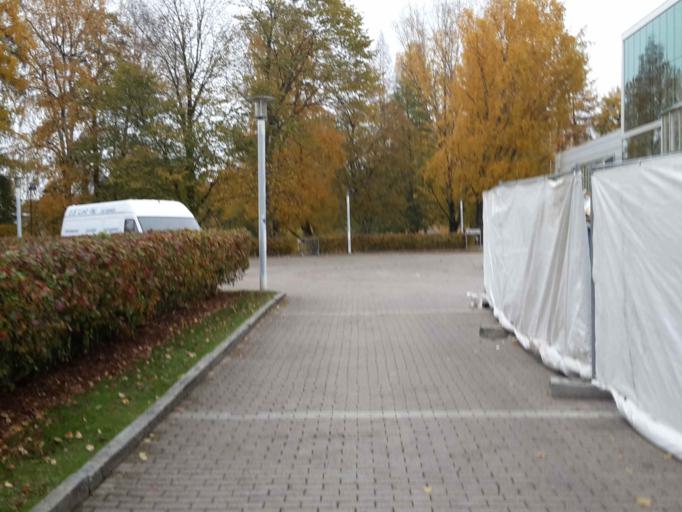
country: FI
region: Pirkanmaa
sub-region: Tampere
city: Tampere
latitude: 61.4963
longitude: 23.7815
